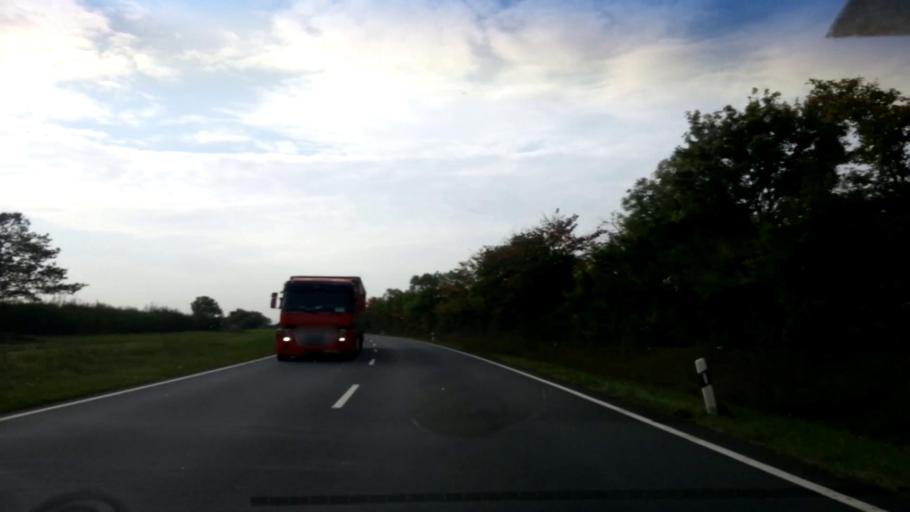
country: DE
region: Bavaria
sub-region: Regierungsbezirk Unterfranken
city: Lulsfeld
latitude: 49.8604
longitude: 10.3502
